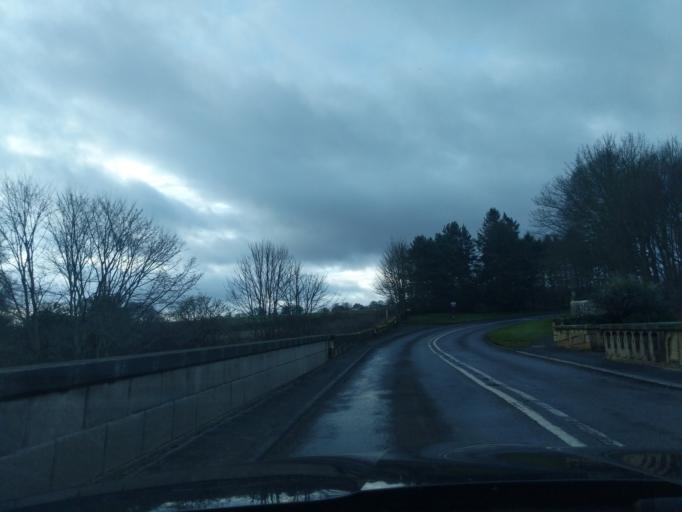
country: GB
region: England
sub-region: Northumberland
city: Alnwick
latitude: 55.4179
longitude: -1.6897
